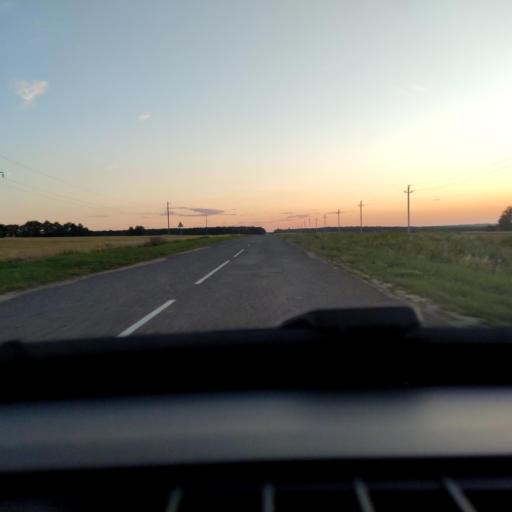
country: RU
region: Lipetsk
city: Zadonsk
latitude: 52.3114
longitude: 38.9077
